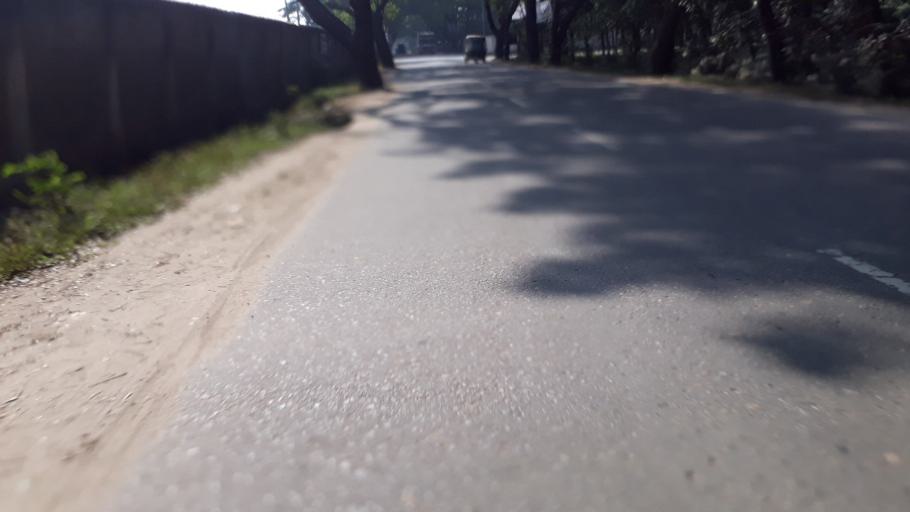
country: BD
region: Dhaka
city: Tungi
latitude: 23.8997
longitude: 90.2750
